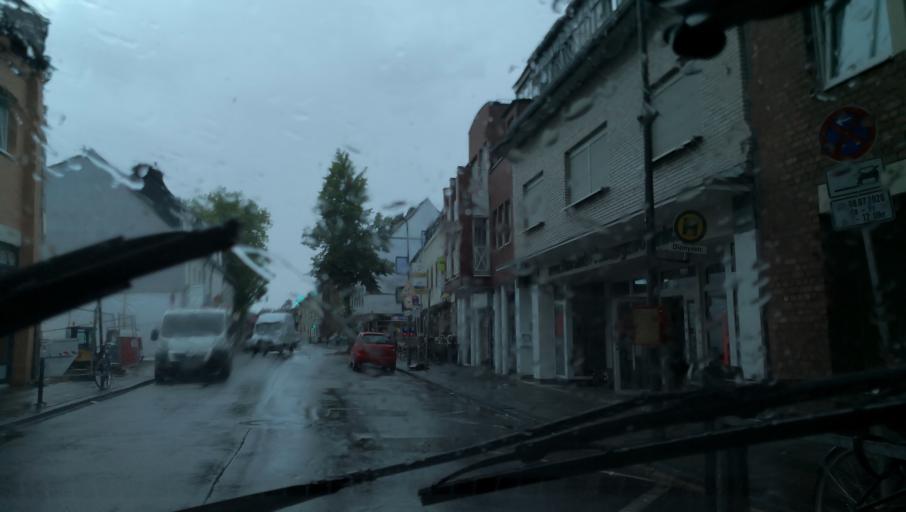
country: DE
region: North Rhine-Westphalia
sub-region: Regierungsbezirk Koln
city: Bilderstoeckchen
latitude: 50.9970
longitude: 6.9062
